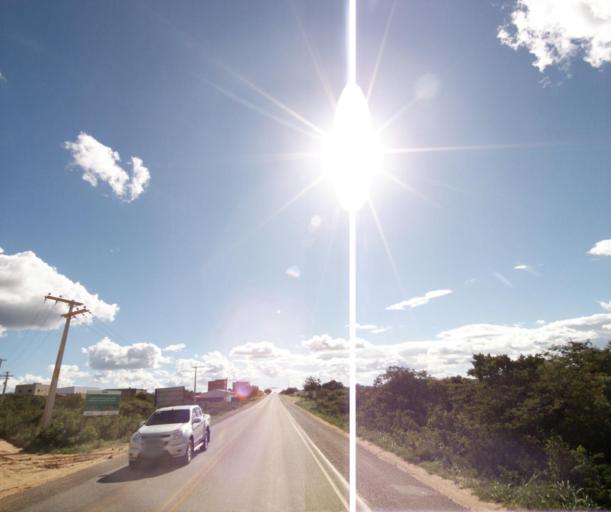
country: BR
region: Bahia
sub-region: Caetite
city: Caetite
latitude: -14.0643
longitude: -42.5241
